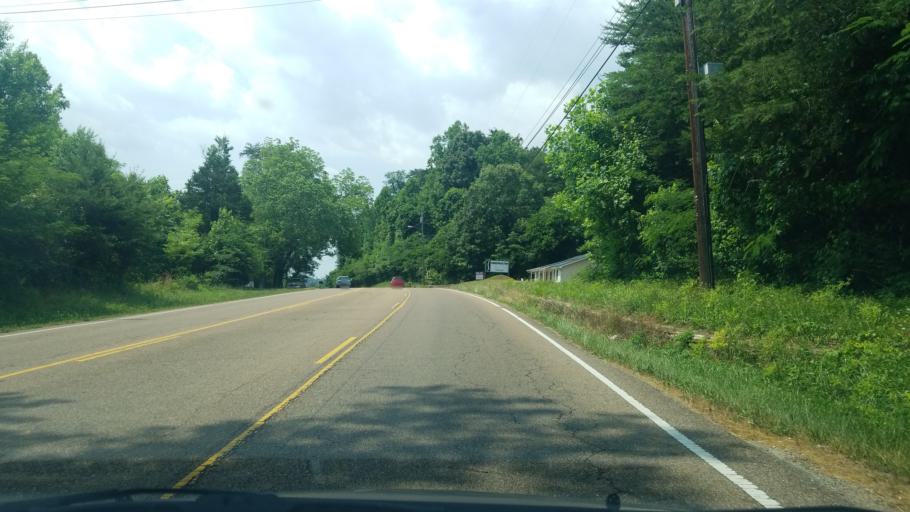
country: US
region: Tennessee
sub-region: Hamilton County
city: Soddy-Daisy
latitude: 35.2526
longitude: -85.1847
